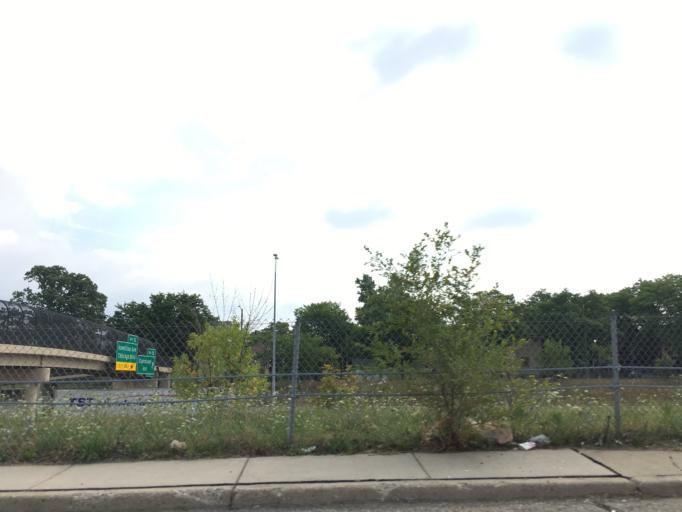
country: US
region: Michigan
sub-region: Wayne County
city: Highland Park
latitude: 42.3768
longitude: -83.0889
